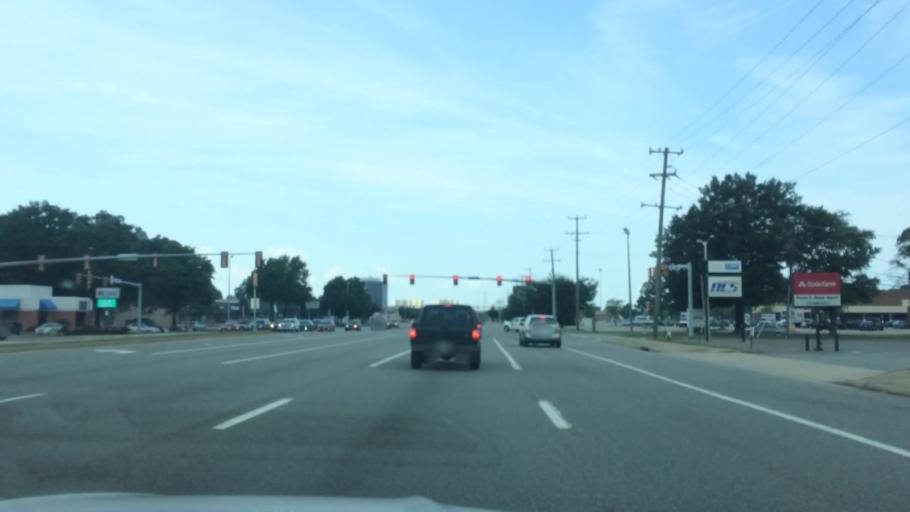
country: US
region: Virginia
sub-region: City of Newport News
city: Newport News
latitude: 37.0243
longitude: -76.4348
